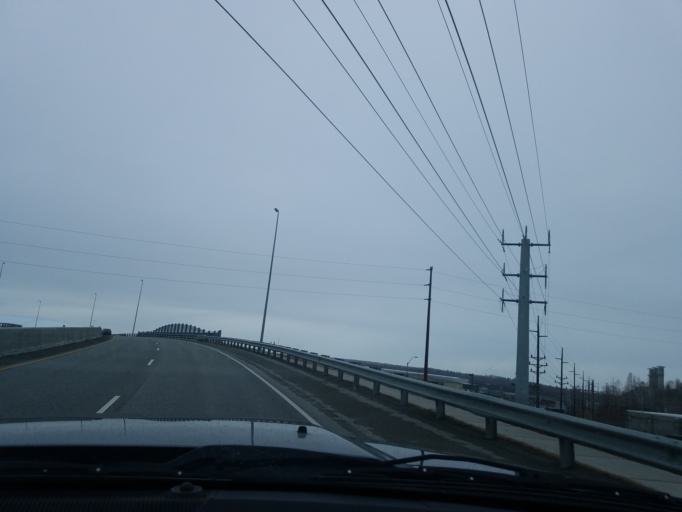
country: US
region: Alaska
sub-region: Anchorage Municipality
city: Anchorage
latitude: 61.1663
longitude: -149.8964
